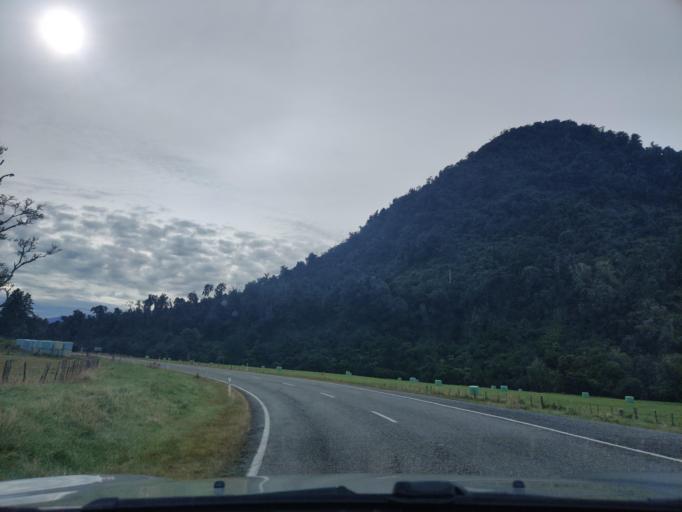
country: NZ
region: West Coast
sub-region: Westland District
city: Hokitika
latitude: -43.2861
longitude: 170.3148
